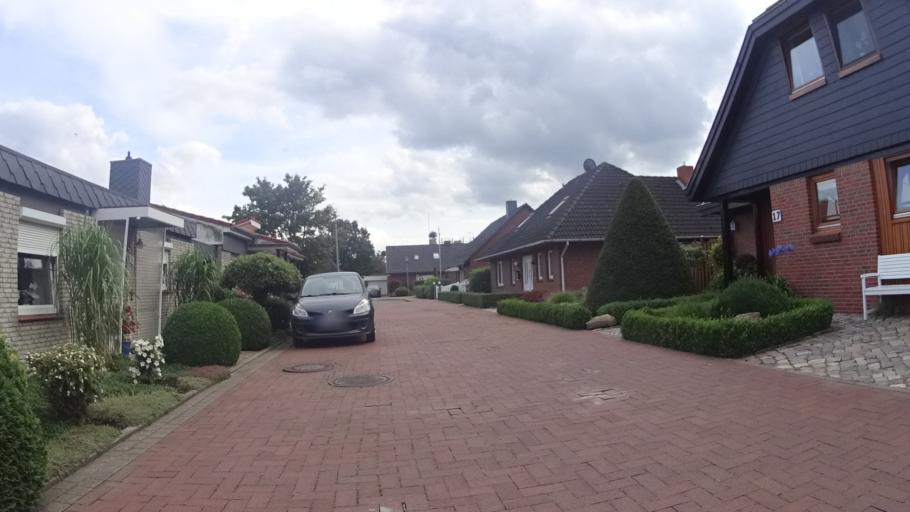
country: DE
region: Schleswig-Holstein
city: Blomesche Wildnis
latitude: 53.7976
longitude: 9.4107
